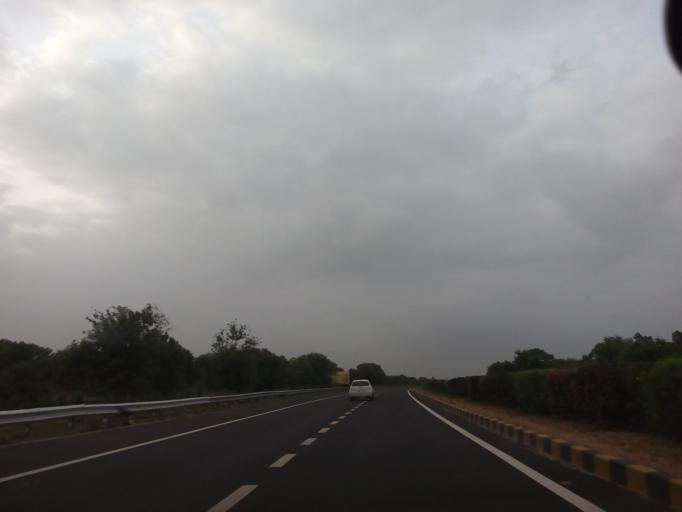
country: IN
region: Gujarat
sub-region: Kheda
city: Mahemdavad
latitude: 22.8790
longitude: 72.7973
